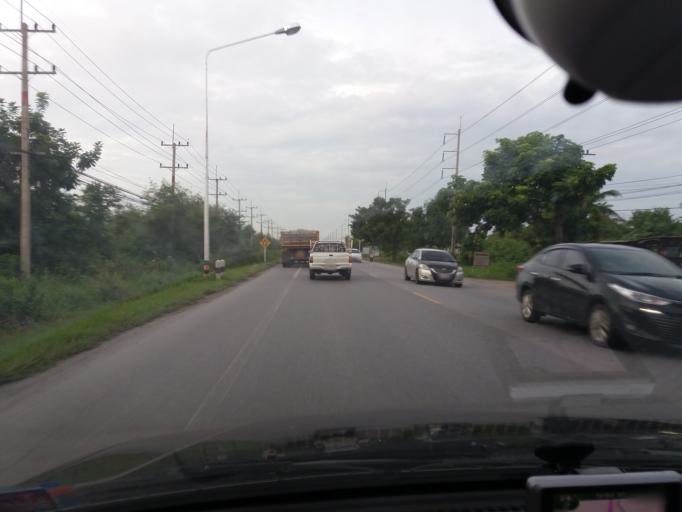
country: TH
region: Suphan Buri
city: U Thong
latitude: 14.4008
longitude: 99.8962
